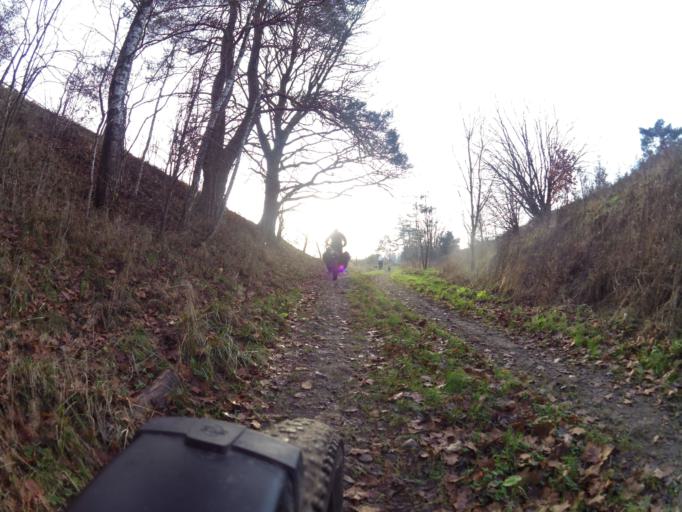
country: PL
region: West Pomeranian Voivodeship
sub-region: Powiat koszalinski
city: Polanow
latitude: 54.2005
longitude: 16.7240
